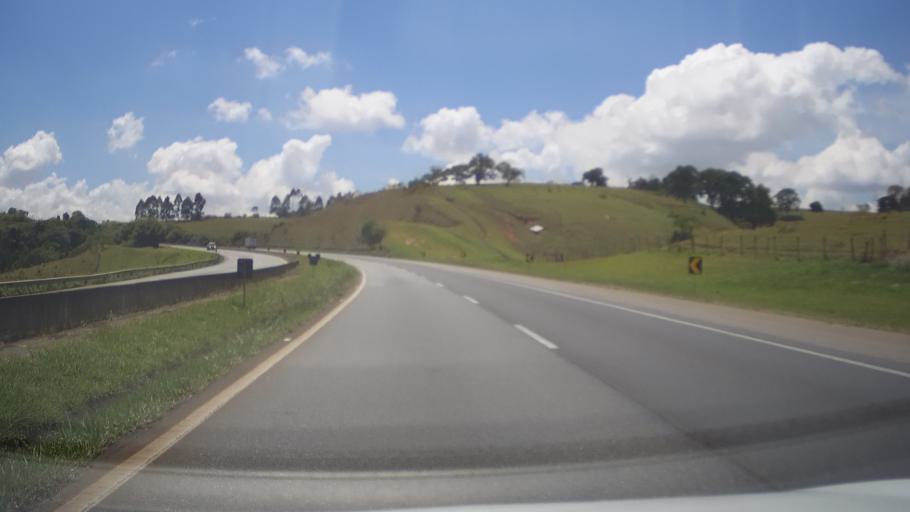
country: BR
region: Minas Gerais
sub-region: Sao Goncalo Do Sapucai
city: Sao Goncalo do Sapucai
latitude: -21.9089
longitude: -45.5638
